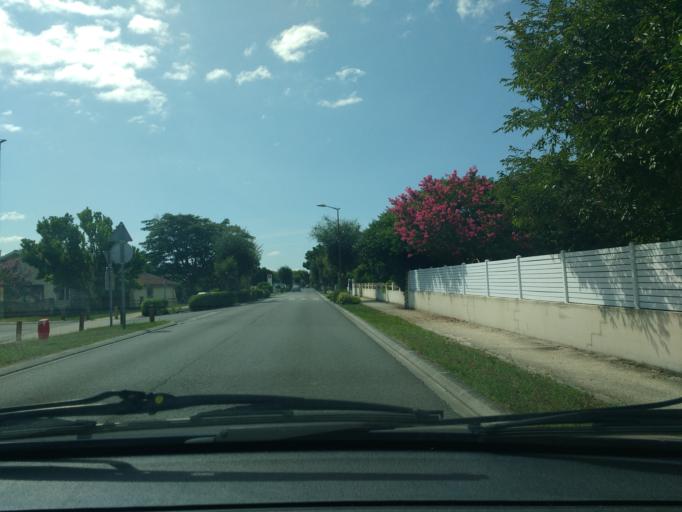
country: FR
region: Aquitaine
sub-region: Departement de la Gironde
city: Salles
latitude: 44.5516
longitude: -0.8615
